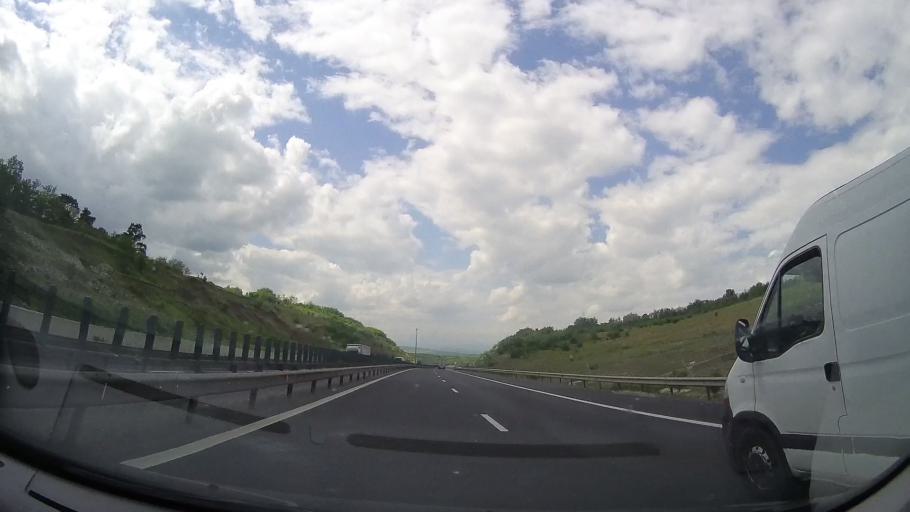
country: RO
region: Sibiu
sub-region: Oras Saliste
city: Saliste
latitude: 45.8185
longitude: 23.8762
